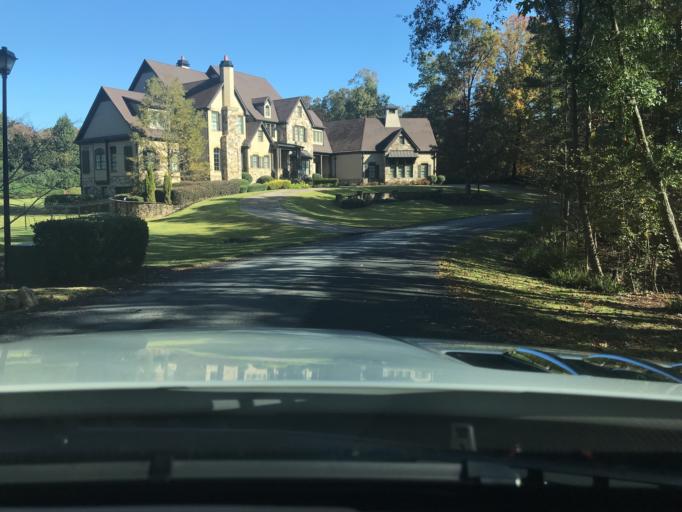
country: US
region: Georgia
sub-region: Gwinnett County
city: Duluth
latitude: 34.0370
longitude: -84.1610
